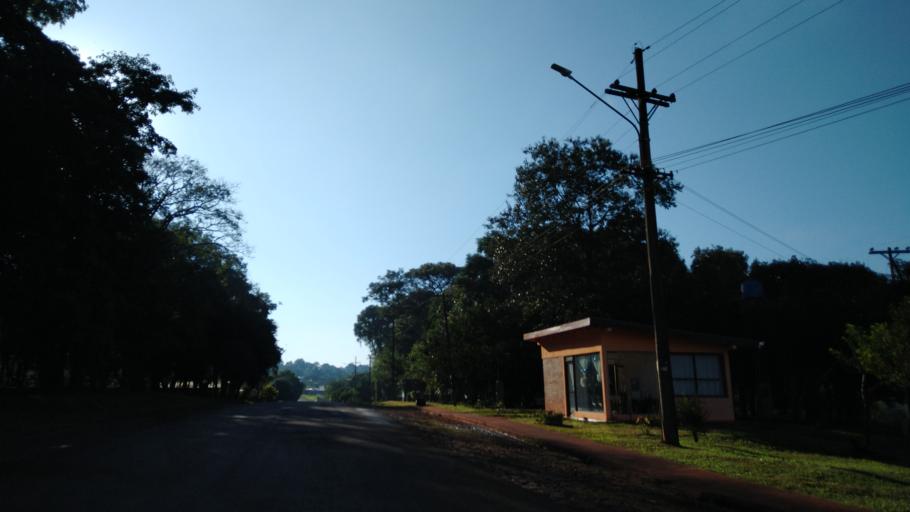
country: AR
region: Misiones
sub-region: Departamento de Montecarlo
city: Montecarlo
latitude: -26.5693
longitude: -54.7735
